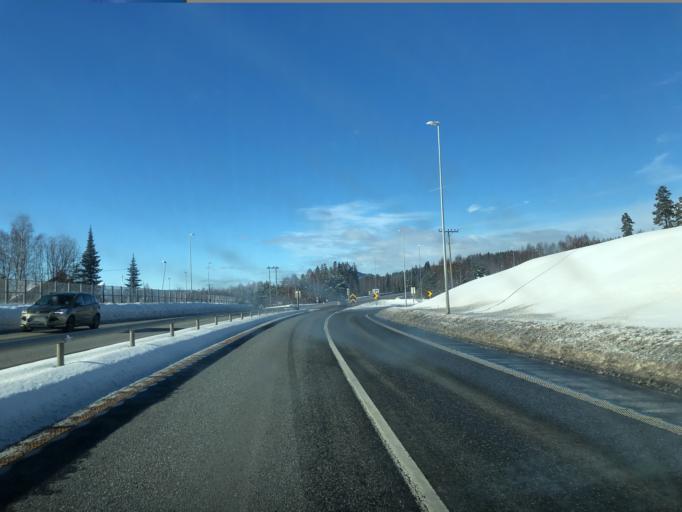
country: NO
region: Oppland
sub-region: Gran
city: Jaren
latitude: 60.3973
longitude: 10.5556
